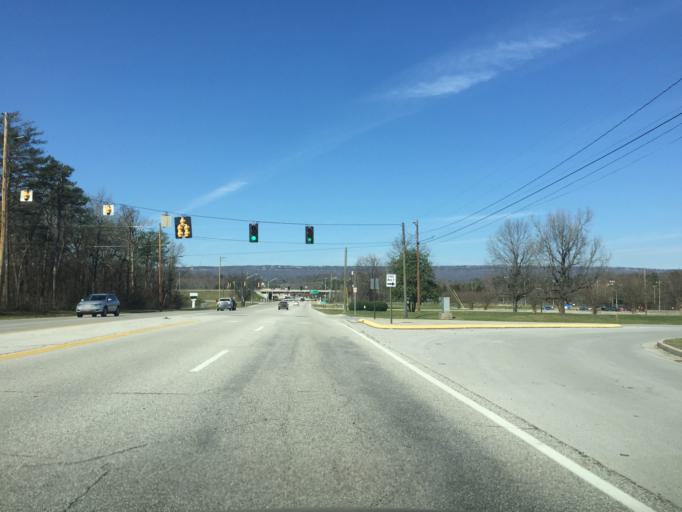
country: US
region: Tennessee
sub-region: Hamilton County
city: East Chattanooga
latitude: 35.1103
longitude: -85.2467
